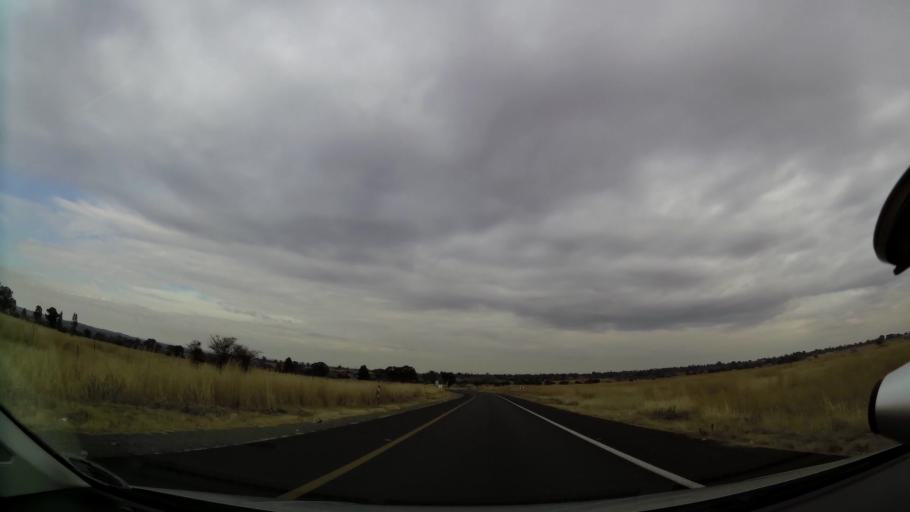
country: ZA
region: Orange Free State
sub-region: Fezile Dabi District Municipality
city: Kroonstad
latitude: -27.6264
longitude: 27.2541
